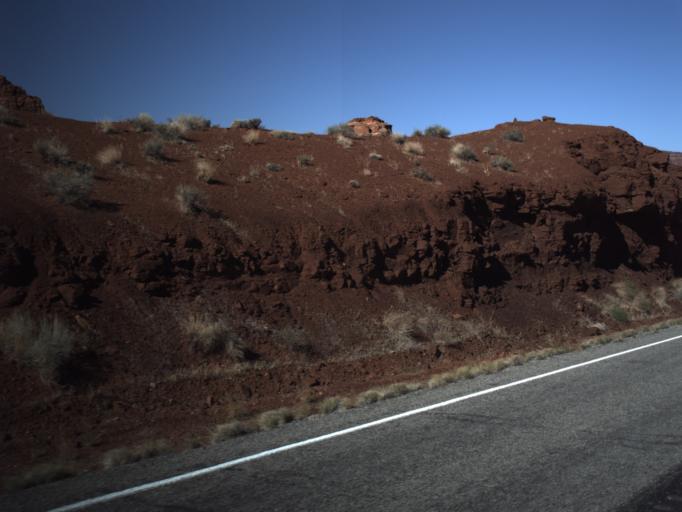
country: US
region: Utah
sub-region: San Juan County
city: Blanding
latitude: 37.8782
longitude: -110.3518
